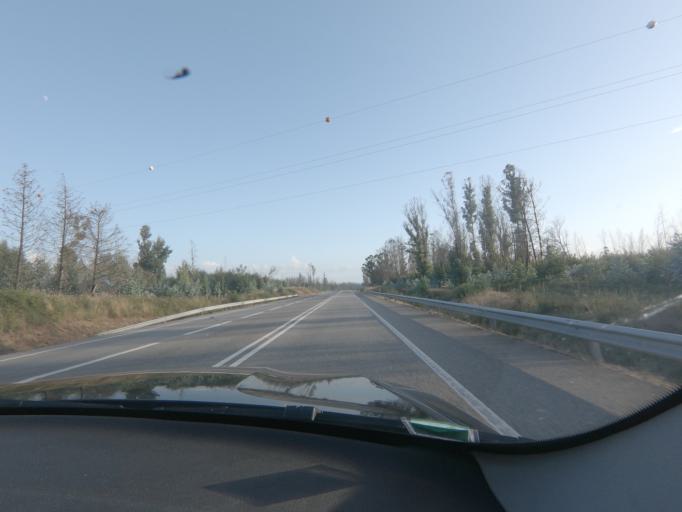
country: PT
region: Viseu
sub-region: Concelho de Tondela
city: Tondela
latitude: 40.4576
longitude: -8.1032
